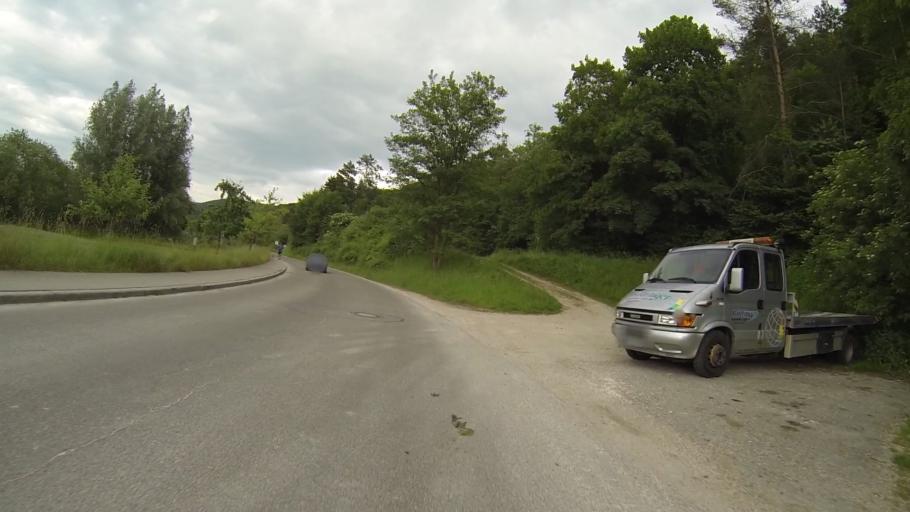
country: DE
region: Baden-Wuerttemberg
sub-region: Tuebingen Region
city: Blaubeuren
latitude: 48.3956
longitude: 9.8045
